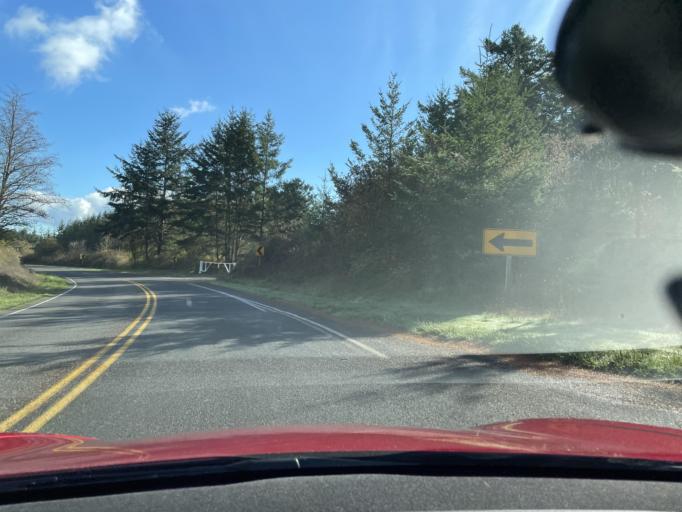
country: US
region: Washington
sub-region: San Juan County
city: Friday Harbor
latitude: 48.4653
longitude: -123.0287
